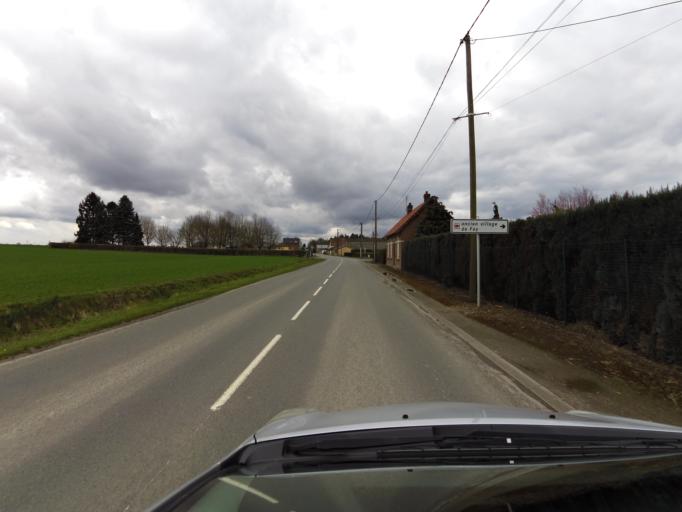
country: FR
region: Picardie
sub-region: Departement de la Somme
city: Chaulnes
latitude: 49.8852
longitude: 2.8096
